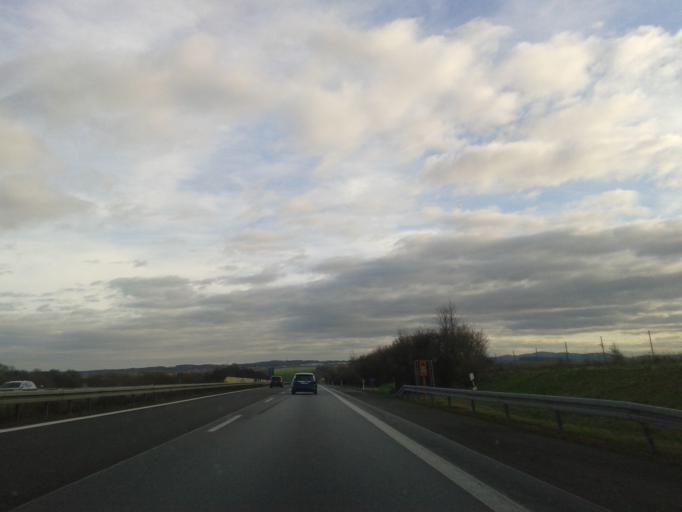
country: DE
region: Saxony
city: Crostwitz
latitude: 51.2024
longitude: 14.2752
